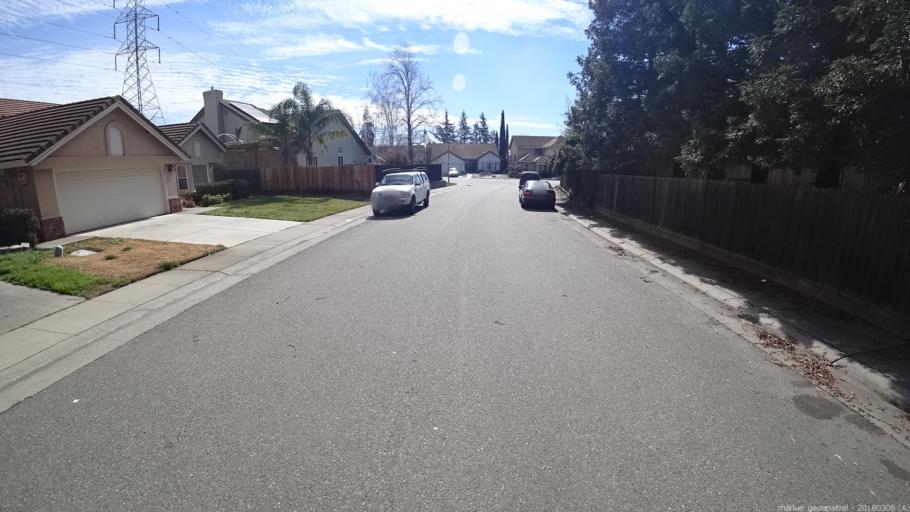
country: US
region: California
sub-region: Sacramento County
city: Vineyard
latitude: 38.4615
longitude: -121.3441
